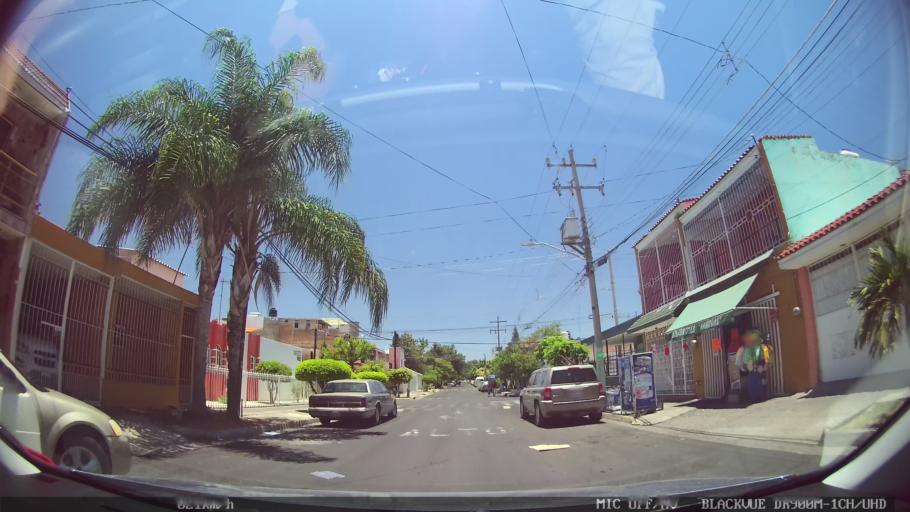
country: MX
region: Jalisco
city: Tlaquepaque
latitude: 20.6753
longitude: -103.2847
